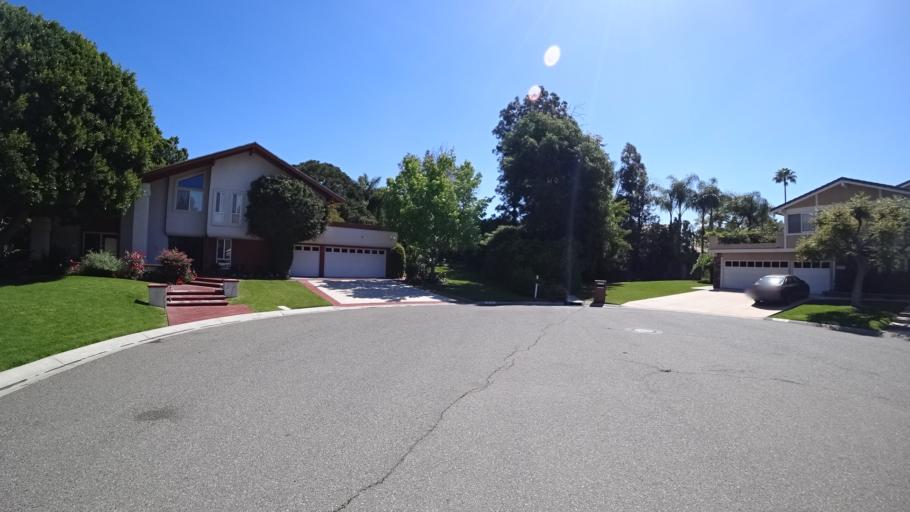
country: US
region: California
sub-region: Orange County
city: Villa Park
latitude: 33.8120
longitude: -117.8160
